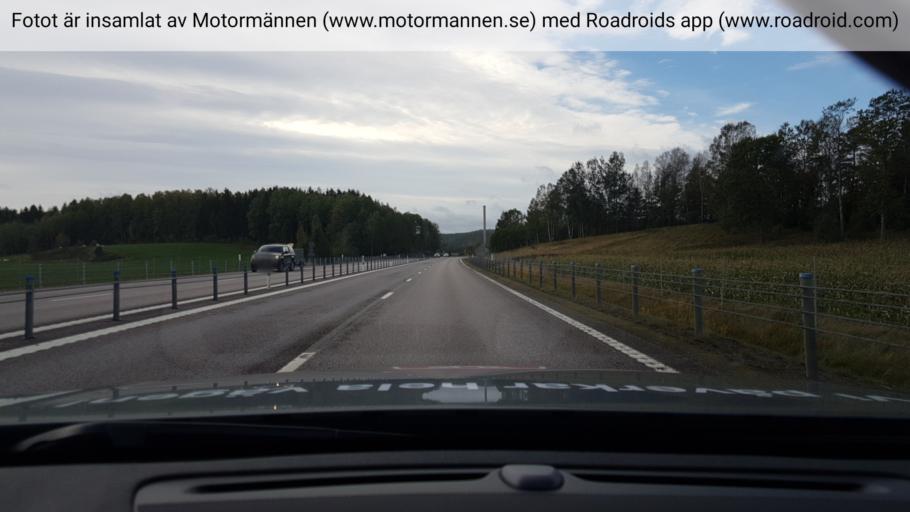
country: SE
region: Vaermland
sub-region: Karlstads Kommun
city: Valberg
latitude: 59.3788
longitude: 13.2006
